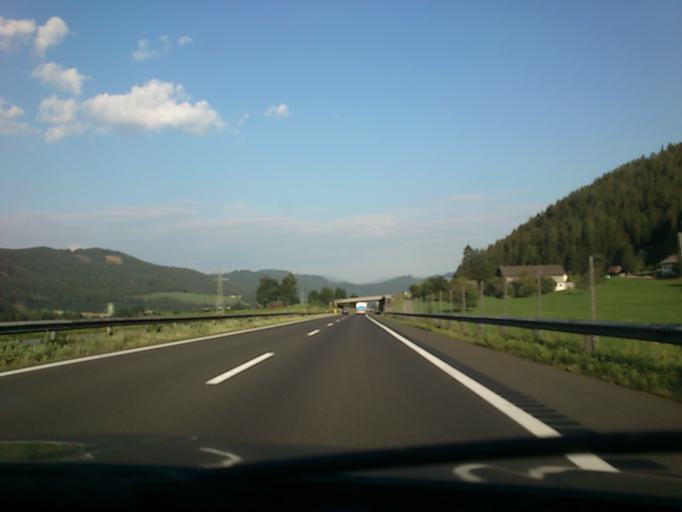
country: AT
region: Styria
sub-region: Politischer Bezirk Leoben
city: Kammern im Liesingtal
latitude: 47.3831
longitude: 14.9329
